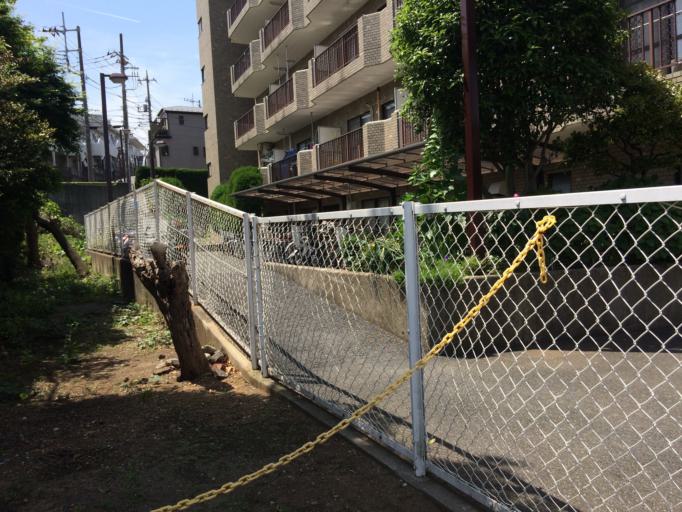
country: JP
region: Tokyo
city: Chofugaoka
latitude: 35.5801
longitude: 139.5947
